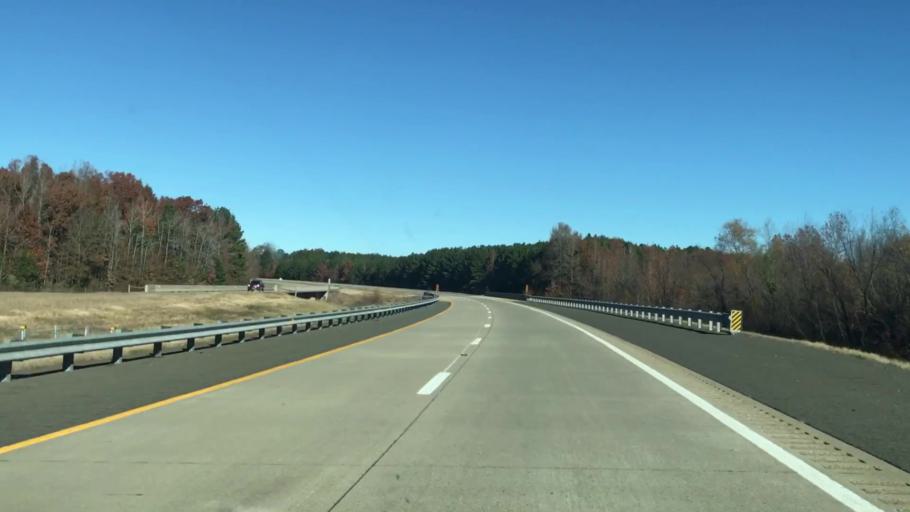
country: US
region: Texas
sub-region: Bowie County
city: Texarkana
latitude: 33.2394
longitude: -93.8731
